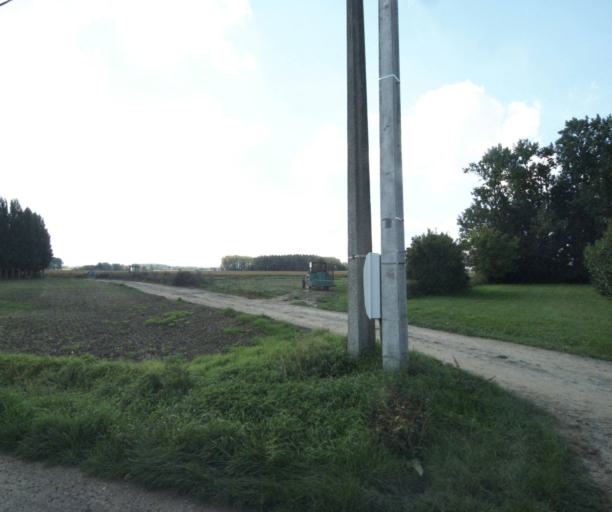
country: FR
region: Nord-Pas-de-Calais
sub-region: Departement du Nord
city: Illies
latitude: 50.5686
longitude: 2.8111
